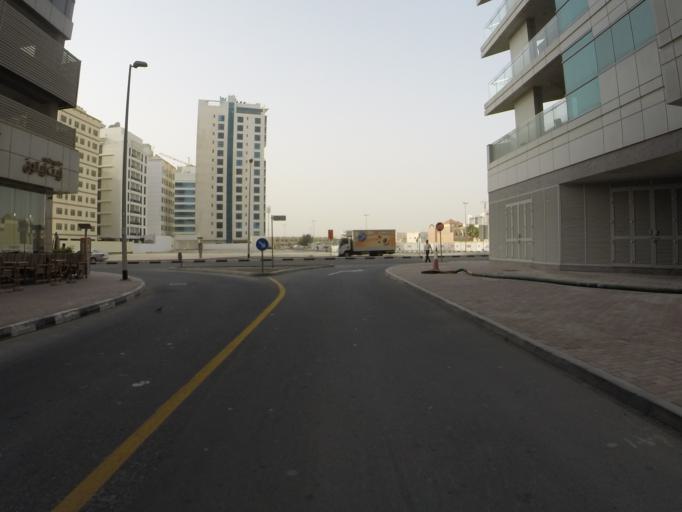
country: AE
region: Dubai
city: Dubai
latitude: 25.1136
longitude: 55.2011
